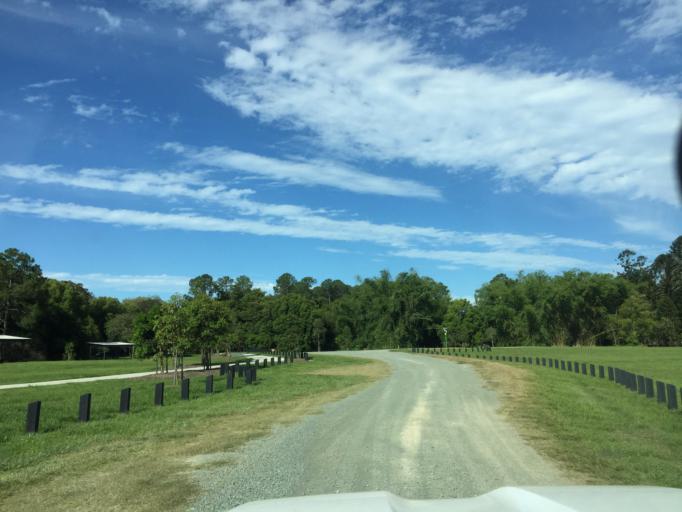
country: AU
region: Queensland
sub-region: Moreton Bay
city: Morayfield
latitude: -27.1063
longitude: 152.9941
